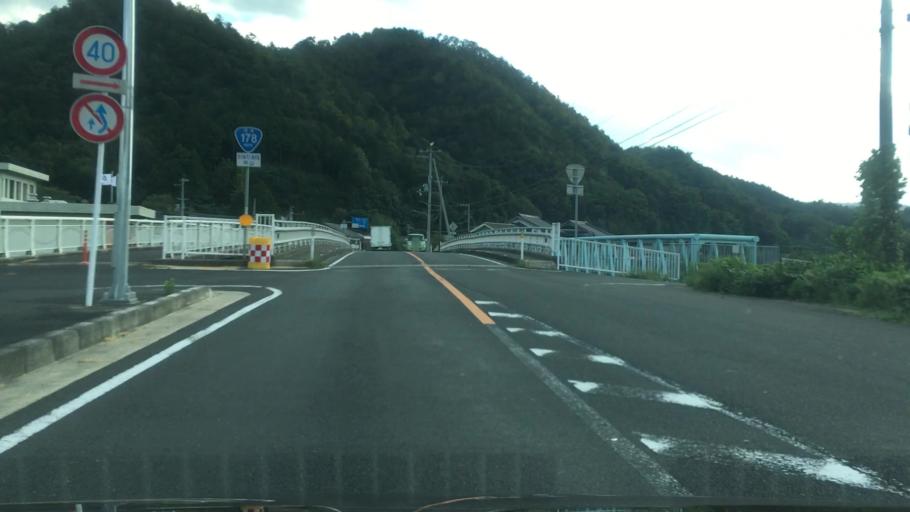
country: JP
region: Hyogo
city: Toyooka
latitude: 35.6090
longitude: 134.9193
